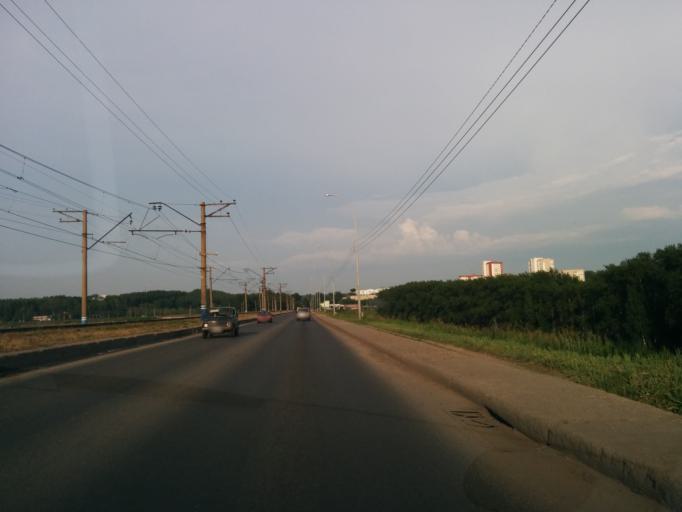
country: RU
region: Perm
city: Perm
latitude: 58.1150
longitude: 56.3537
